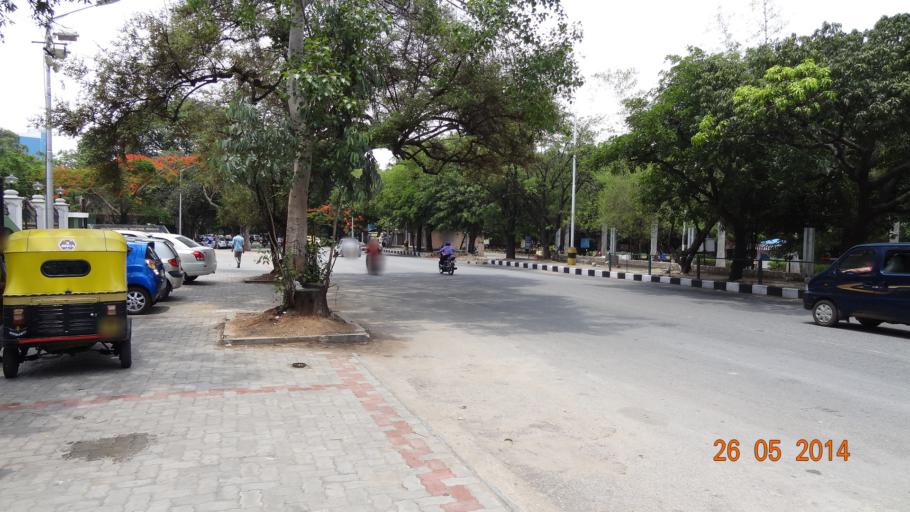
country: IN
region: Karnataka
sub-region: Bangalore Urban
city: Bangalore
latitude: 12.9851
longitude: 77.5904
